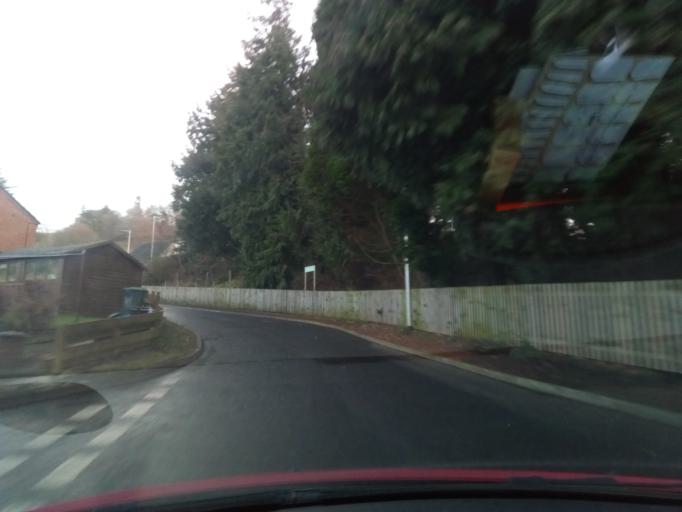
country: GB
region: Scotland
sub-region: The Scottish Borders
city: Hawick
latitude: 55.4293
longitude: -2.7679
